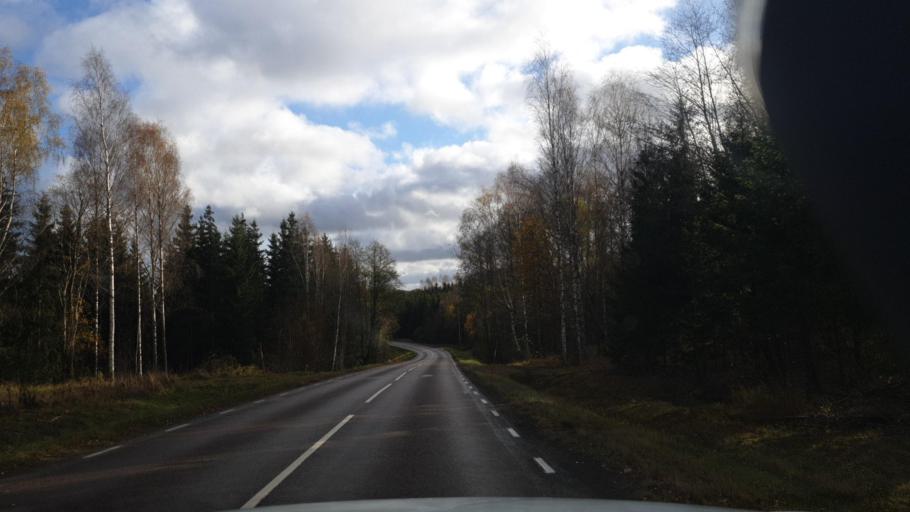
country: SE
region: Vaermland
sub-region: Grums Kommun
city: Slottsbron
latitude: 59.4457
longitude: 12.8606
